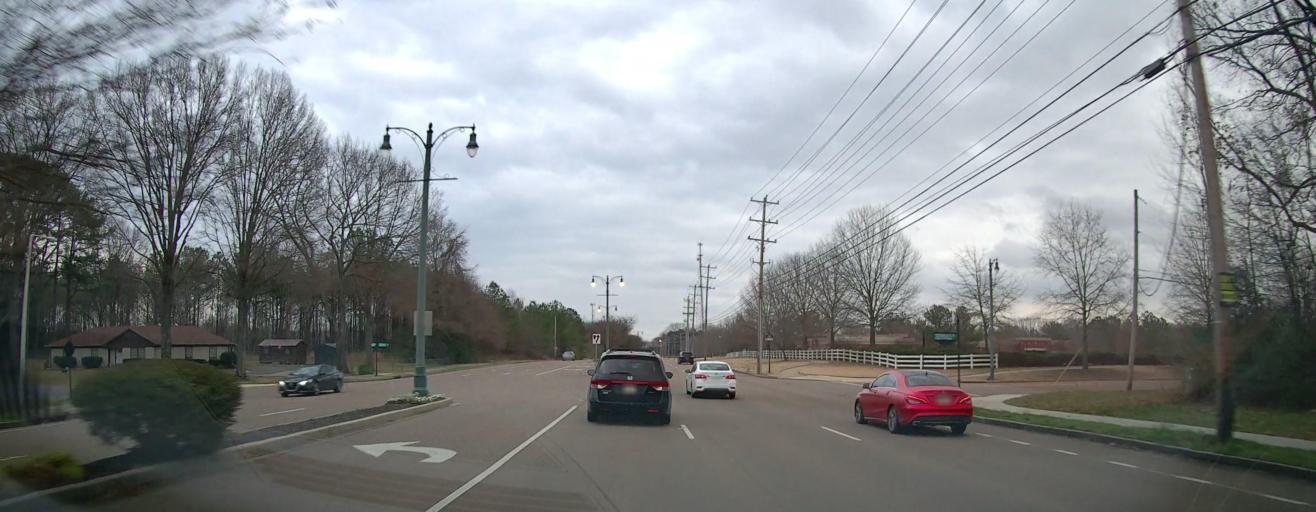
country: US
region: Tennessee
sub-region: Shelby County
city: Germantown
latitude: 35.0474
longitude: -89.7480
